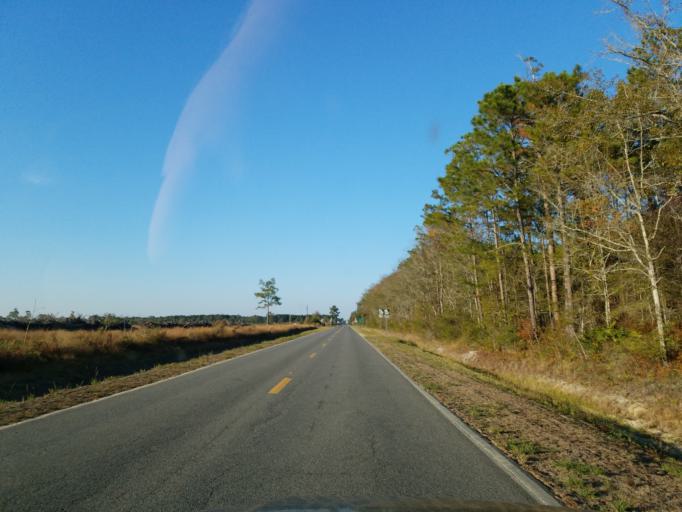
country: US
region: Georgia
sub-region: Lanier County
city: Lakeland
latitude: 31.1607
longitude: -83.0875
